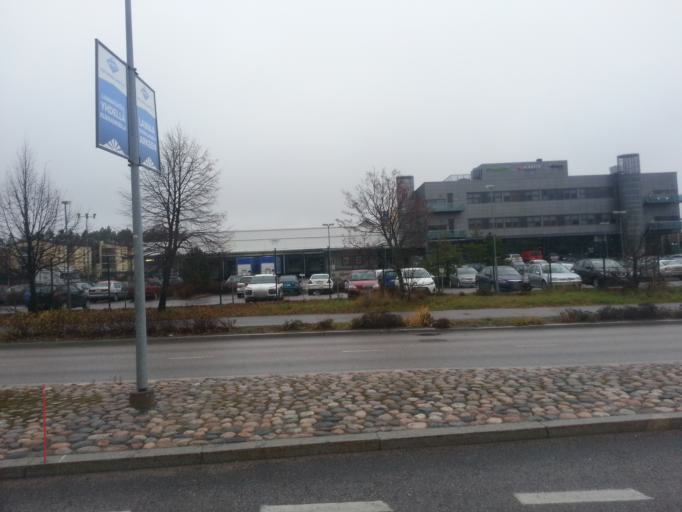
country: FI
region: Uusimaa
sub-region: Helsinki
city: Vantaa
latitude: 60.2898
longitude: 24.9535
